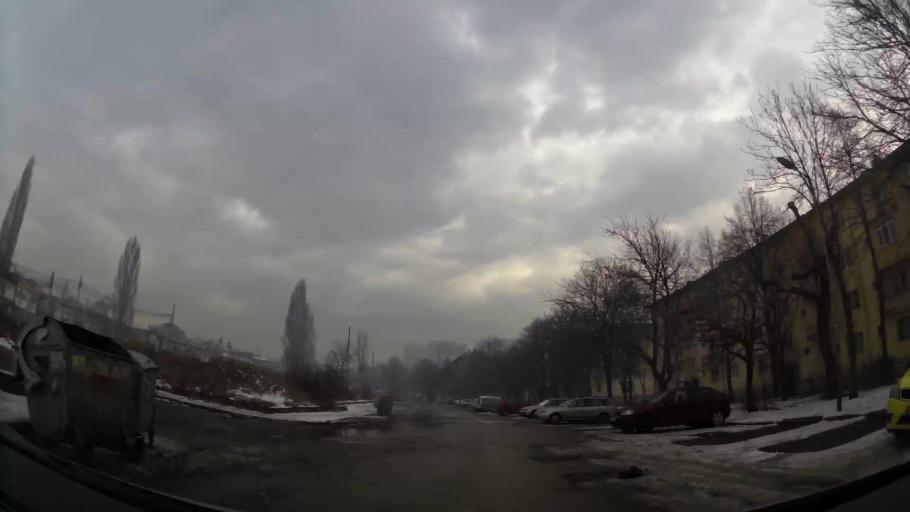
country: BG
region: Sofia-Capital
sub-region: Stolichna Obshtina
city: Sofia
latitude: 42.6935
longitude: 23.2771
